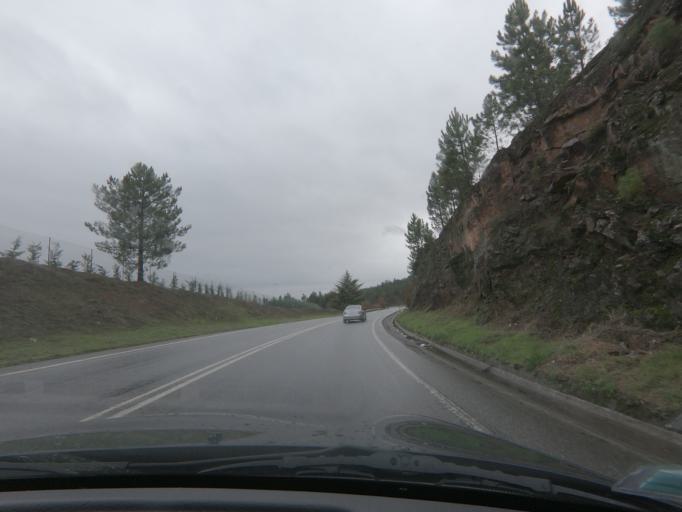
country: PT
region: Braga
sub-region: Celorico de Basto
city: Celorico de Basto
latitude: 41.3307
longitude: -8.0384
